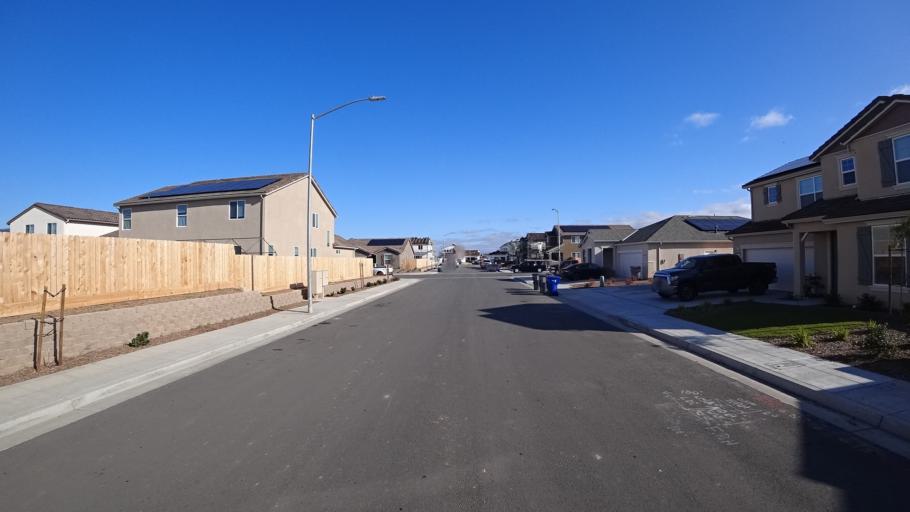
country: US
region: California
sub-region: Fresno County
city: West Park
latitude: 36.8029
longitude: -119.9034
